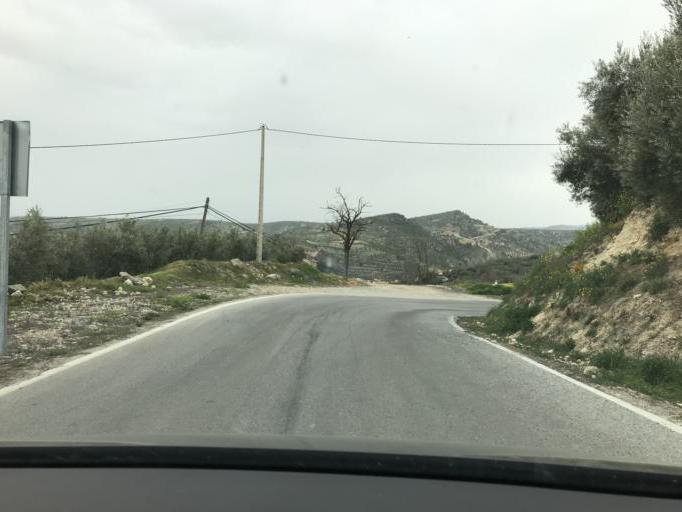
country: ES
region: Andalusia
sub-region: Provincia de Granada
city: Castril
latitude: 37.8002
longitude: -2.7706
